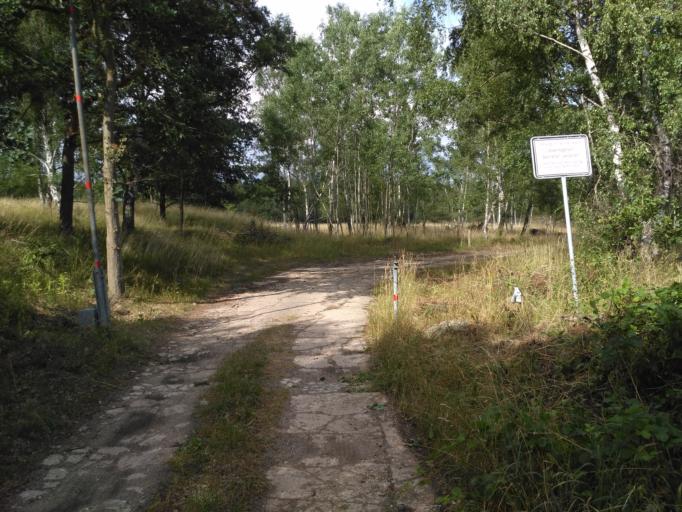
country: DE
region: Saxony
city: Tauscha
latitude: 51.3028
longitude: 13.8403
